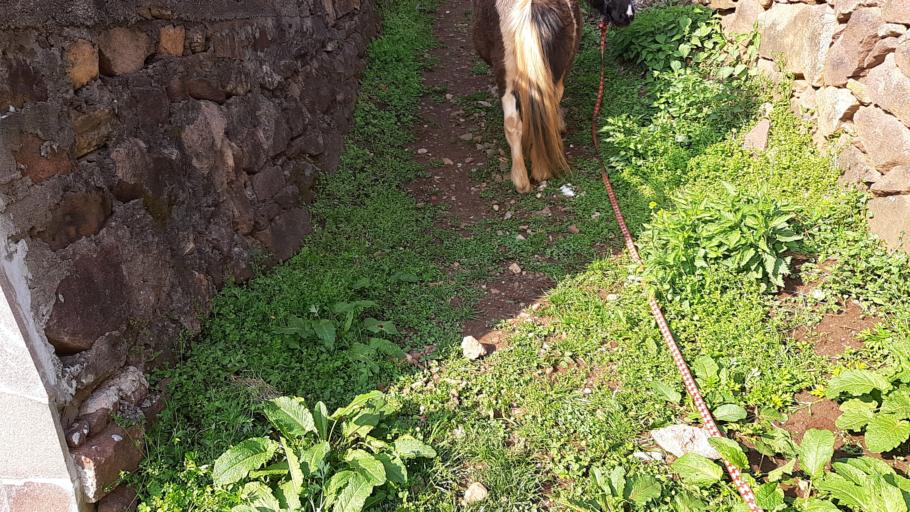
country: IT
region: Trentino-Alto Adige
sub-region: Provincia di Trento
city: Lavis
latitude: 46.1457
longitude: 11.1133
